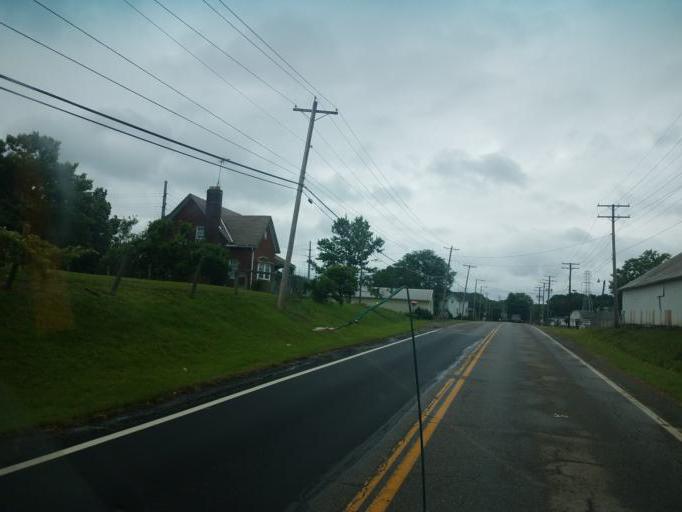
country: US
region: Ohio
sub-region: Carroll County
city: Carrollton
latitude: 40.5844
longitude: -81.0828
